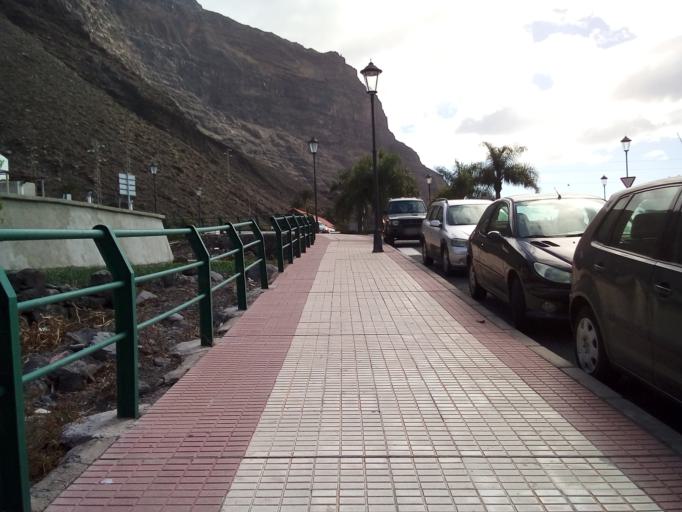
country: ES
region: Canary Islands
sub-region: Provincia de Santa Cruz de Tenerife
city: Alajero
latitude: 28.0946
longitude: -17.3361
